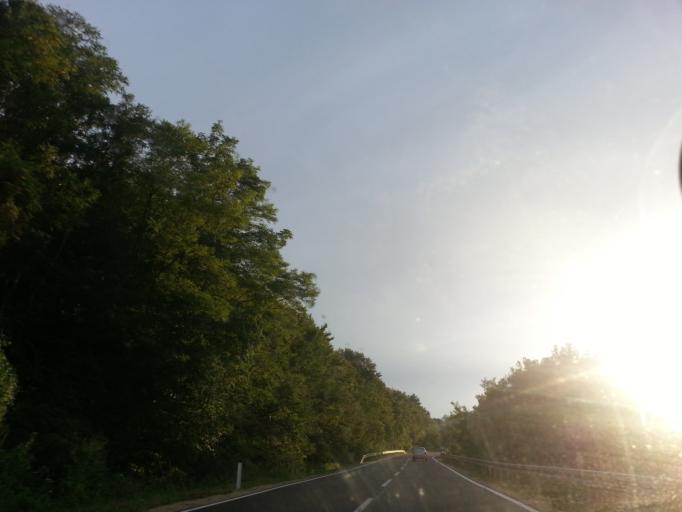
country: HR
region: Vukovarsko-Srijemska
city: Gunja
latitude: 44.8504
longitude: 18.8954
